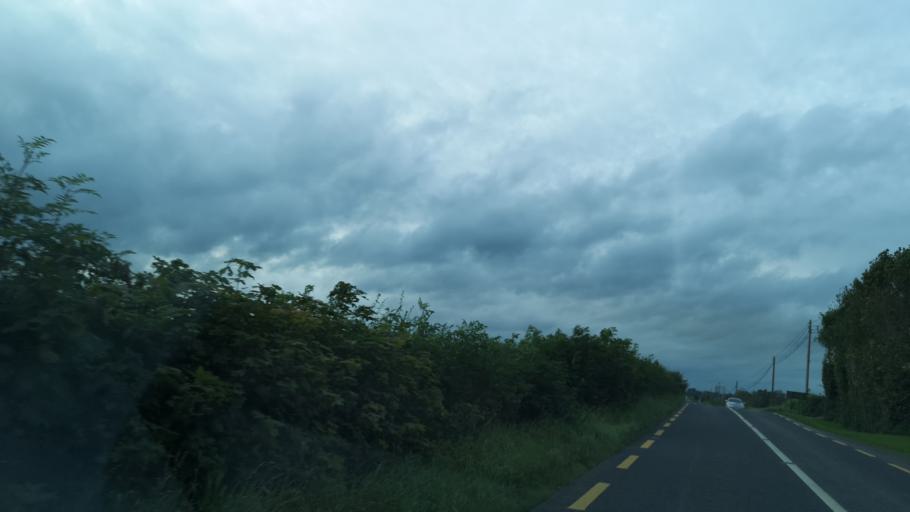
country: IE
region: Leinster
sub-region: Uibh Fhaili
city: Ferbane
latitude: 53.3652
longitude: -7.8539
